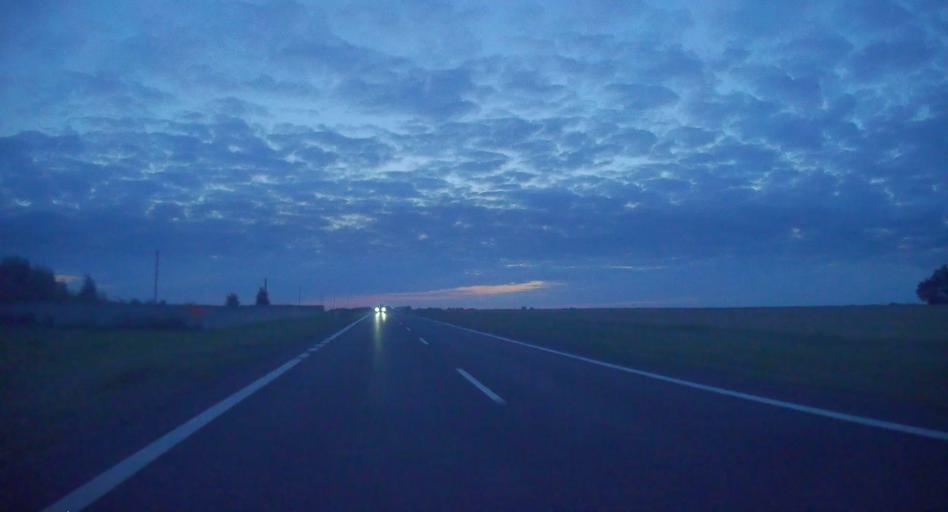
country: PL
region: Silesian Voivodeship
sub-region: Powiat klobucki
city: Klobuck
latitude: 50.8893
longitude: 18.9699
